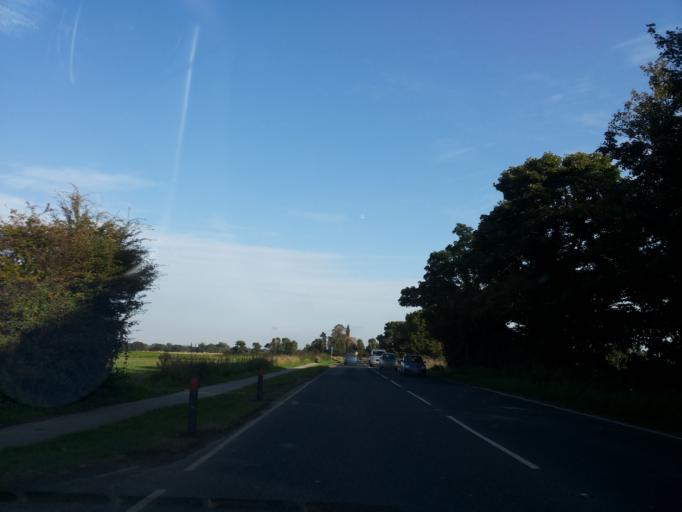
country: GB
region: England
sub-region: East Riding of Yorkshire
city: Snaith
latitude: 53.6873
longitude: -1.0064
